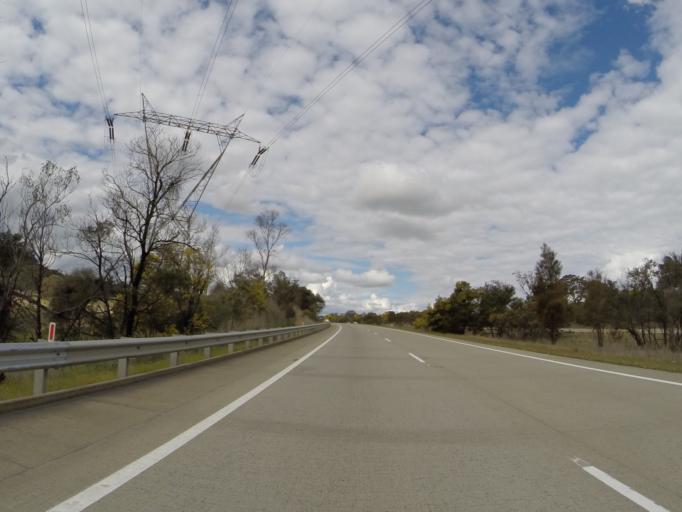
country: AU
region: New South Wales
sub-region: Yass Valley
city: Gundaroo
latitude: -34.8213
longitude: 149.3909
